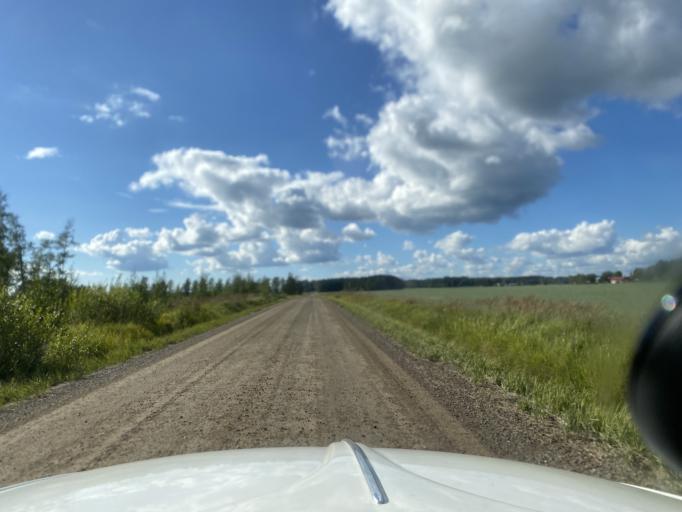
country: FI
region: Pirkanmaa
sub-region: Lounais-Pirkanmaa
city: Punkalaidun
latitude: 61.1330
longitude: 23.2326
